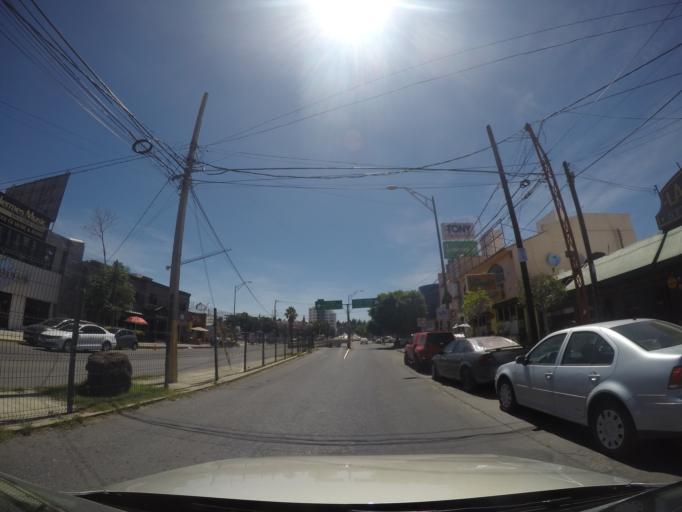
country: MX
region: San Luis Potosi
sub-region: San Luis Potosi
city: San Luis Potosi
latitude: 22.1486
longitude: -101.0134
